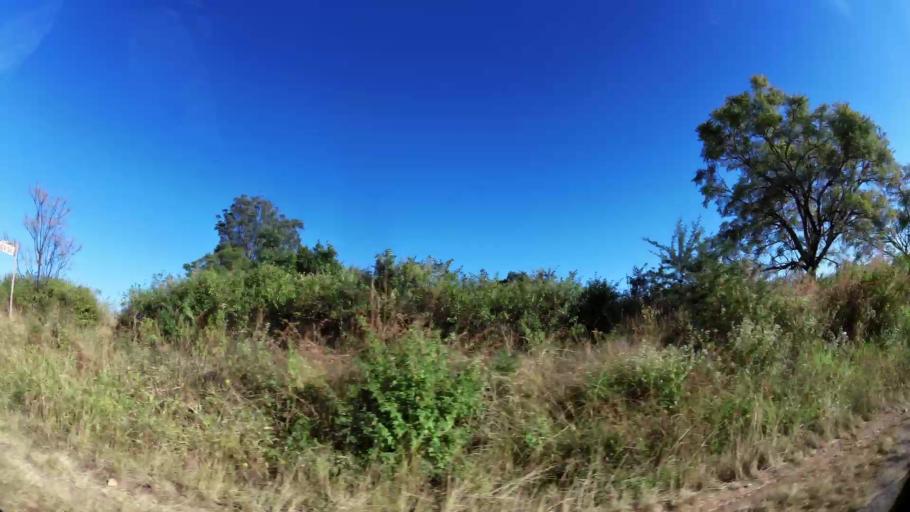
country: ZA
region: Limpopo
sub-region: Mopani District Municipality
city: Tzaneen
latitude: -23.8626
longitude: 30.1086
